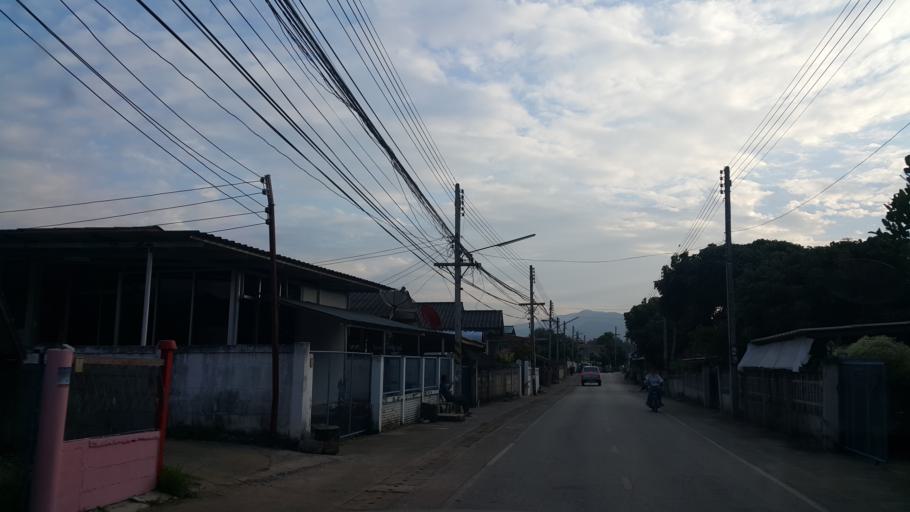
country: TH
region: Lampang
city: Sop Prap
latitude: 17.8760
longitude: 99.3331
